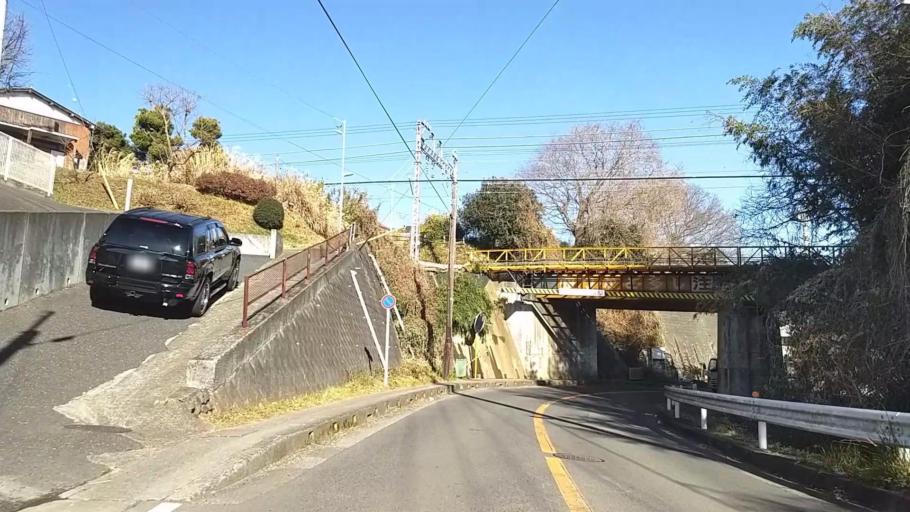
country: JP
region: Kanagawa
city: Hadano
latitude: 35.3648
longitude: 139.2327
